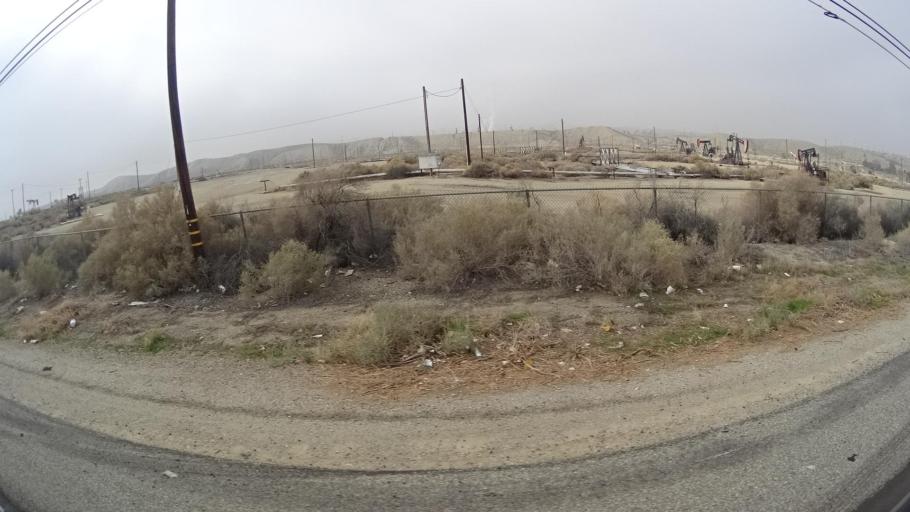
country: US
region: California
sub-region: Kern County
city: Maricopa
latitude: 35.0703
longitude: -119.4021
